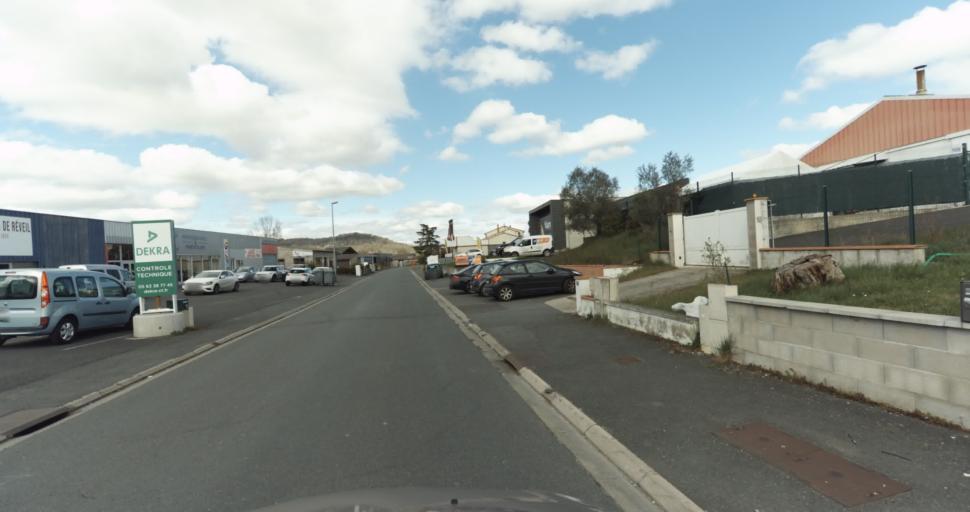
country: FR
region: Midi-Pyrenees
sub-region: Departement du Tarn
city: Puygouzon
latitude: 43.8913
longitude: 2.1621
